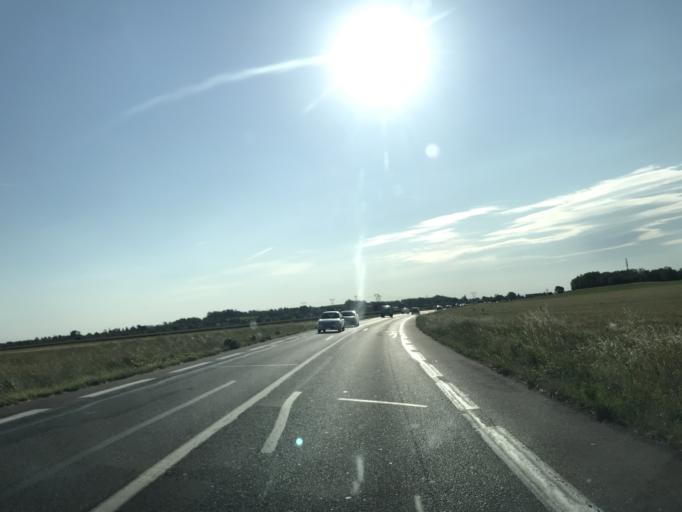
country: FR
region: Rhone-Alpes
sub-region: Departement du Rhone
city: Mions
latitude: 45.6530
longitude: 4.9356
